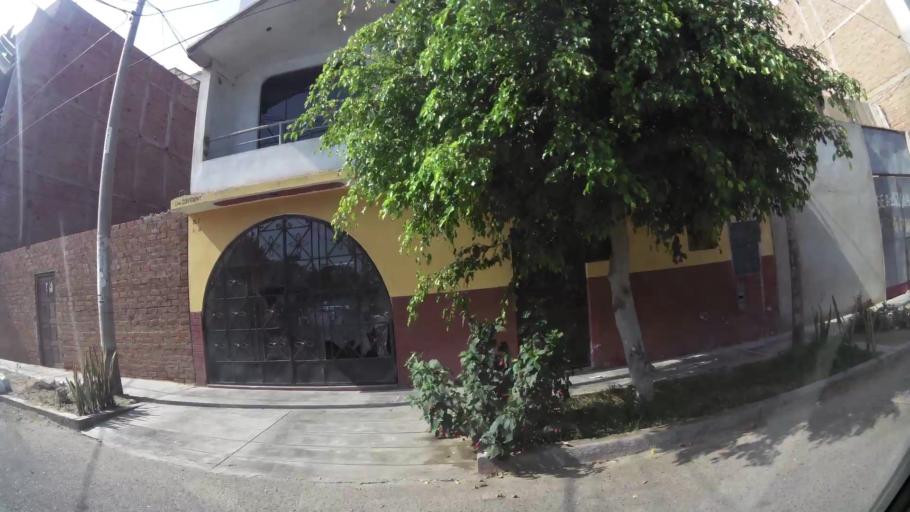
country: PE
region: La Libertad
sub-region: Provincia de Trujillo
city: Trujillo
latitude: -8.1217
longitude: -79.0170
